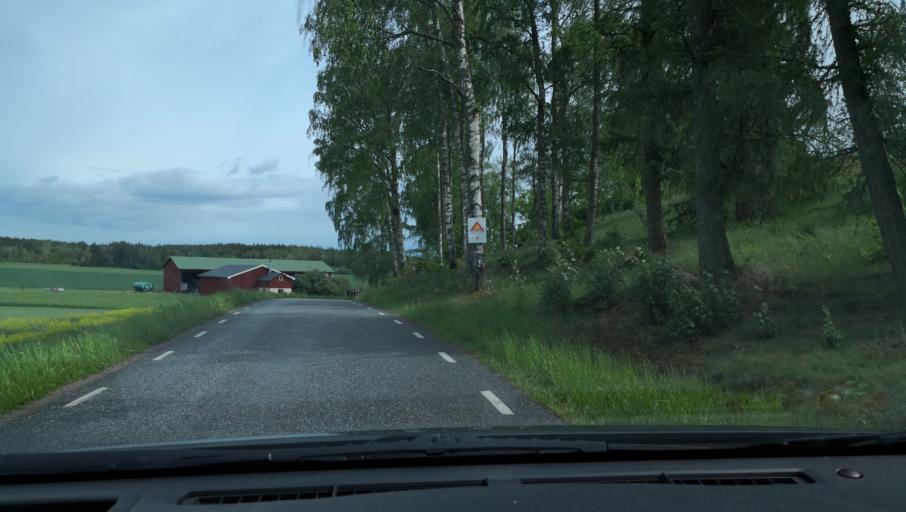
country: SE
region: Uppsala
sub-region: Enkopings Kommun
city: Orsundsbro
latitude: 59.7052
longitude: 17.4108
